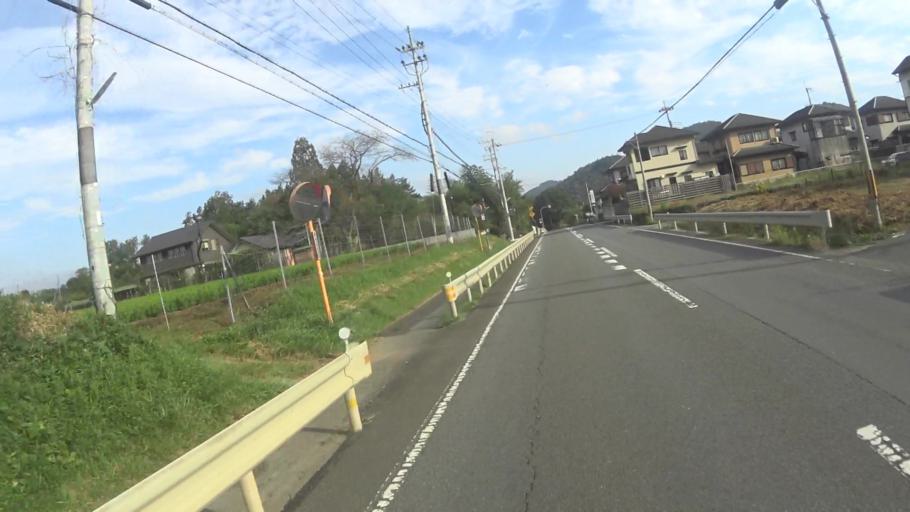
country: JP
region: Kyoto
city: Ayabe
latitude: 35.1707
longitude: 135.4244
